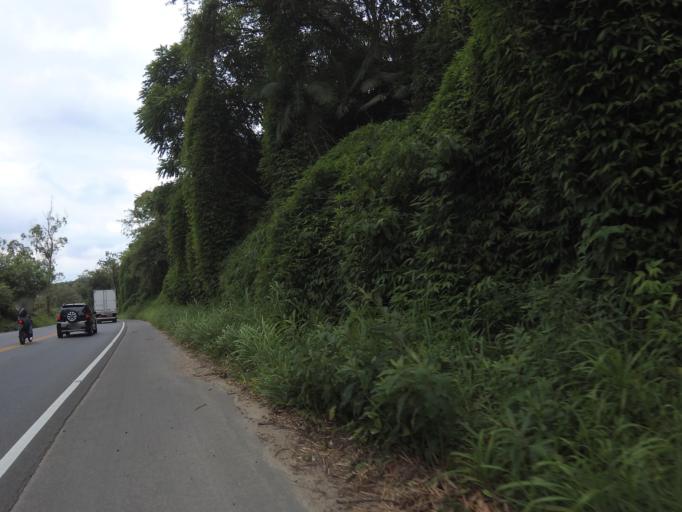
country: BR
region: Santa Catarina
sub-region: Indaial
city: Indaial
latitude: -26.8389
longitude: -49.1647
